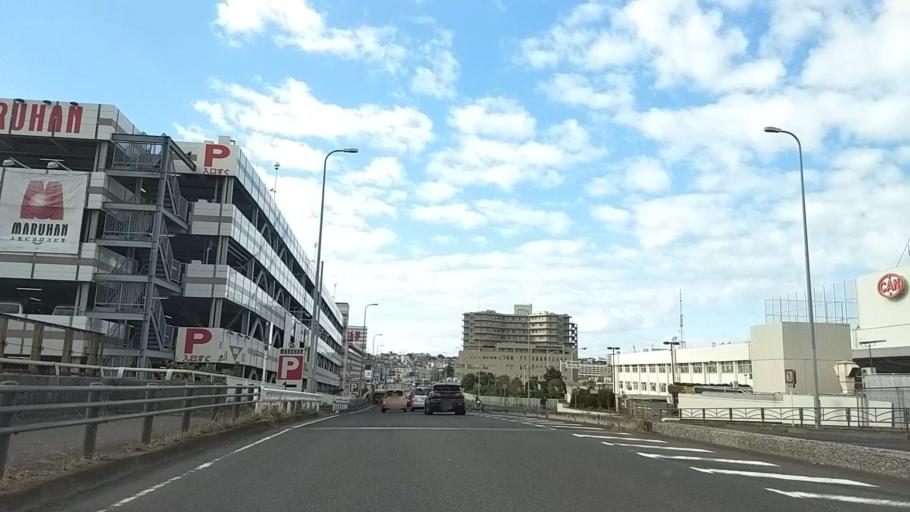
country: JP
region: Kanagawa
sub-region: Kawasaki-shi
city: Kawasaki
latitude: 35.5248
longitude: 139.6798
